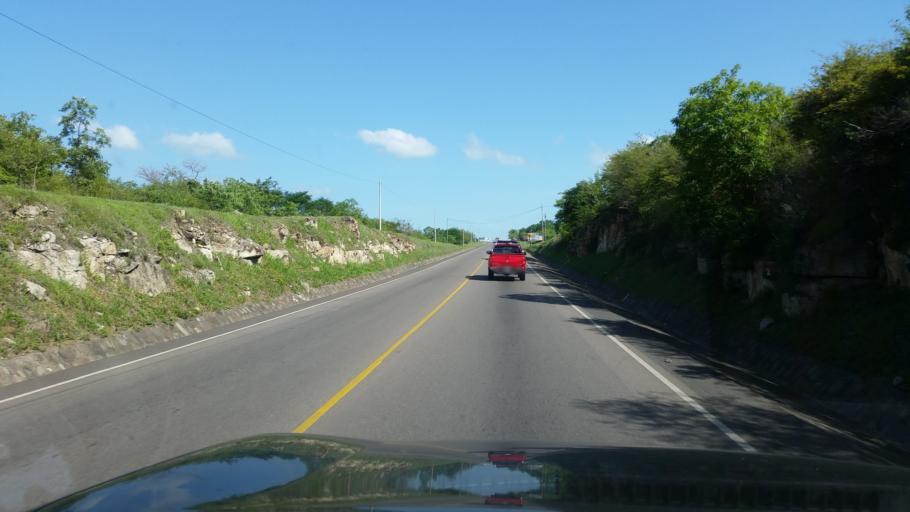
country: NI
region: Matagalpa
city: Ciudad Dario
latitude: 12.7214
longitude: -86.1011
